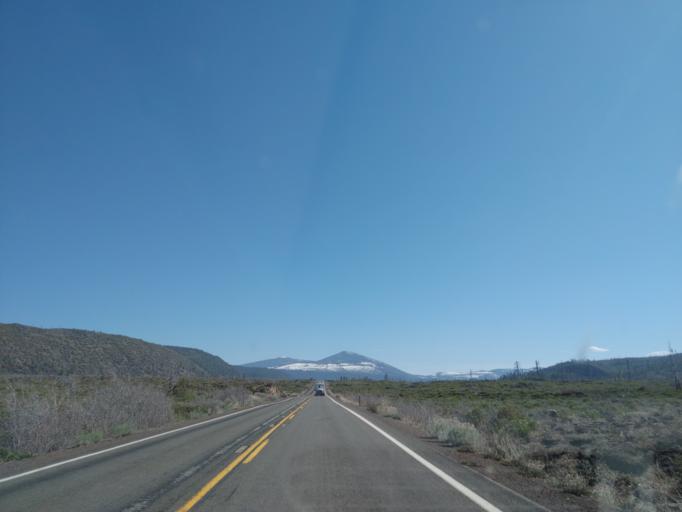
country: US
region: California
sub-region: Shasta County
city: Burney
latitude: 40.7190
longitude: -121.4244
